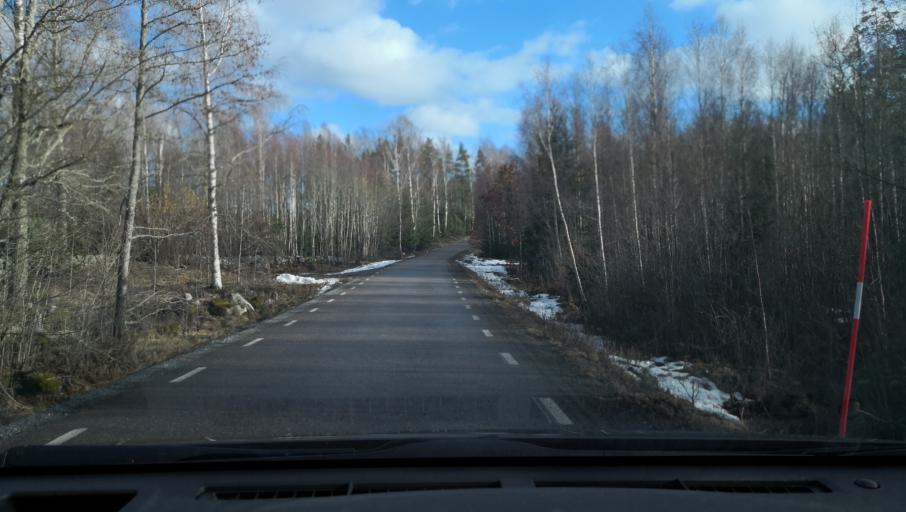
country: SE
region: Vaestmanland
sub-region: Arboga Kommun
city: Arboga
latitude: 59.3278
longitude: 15.7540
